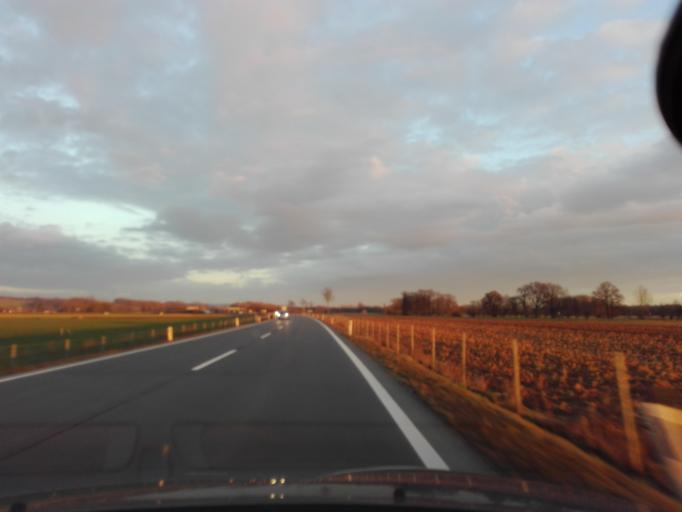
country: AT
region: Upper Austria
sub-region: Politischer Bezirk Perg
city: Perg
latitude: 48.2350
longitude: 14.6291
